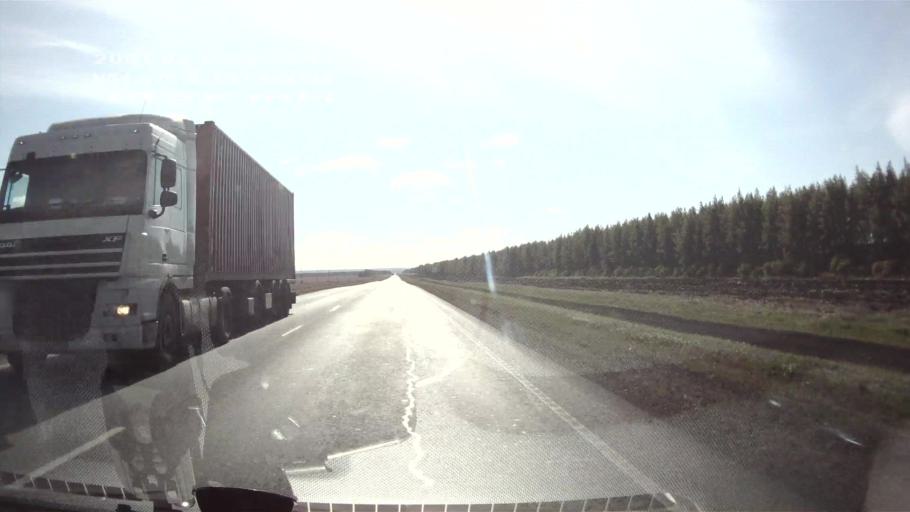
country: RU
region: Ulyanovsk
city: Tsil'na
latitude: 54.5753
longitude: 47.9014
